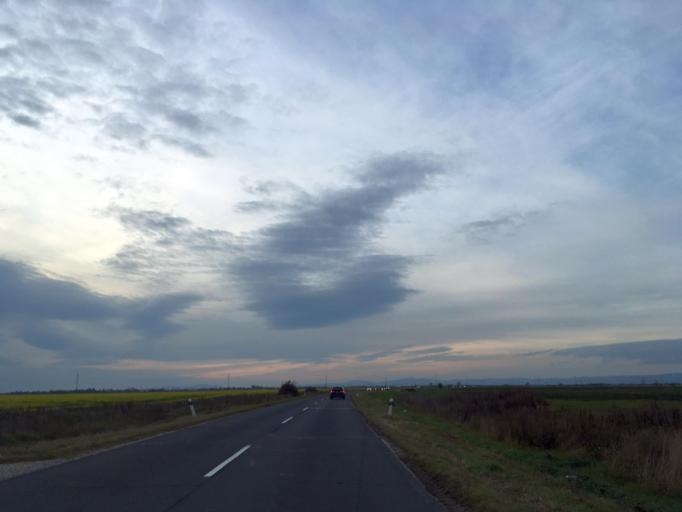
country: SK
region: Trnavsky
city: Samorin
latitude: 48.1044
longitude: 17.3409
